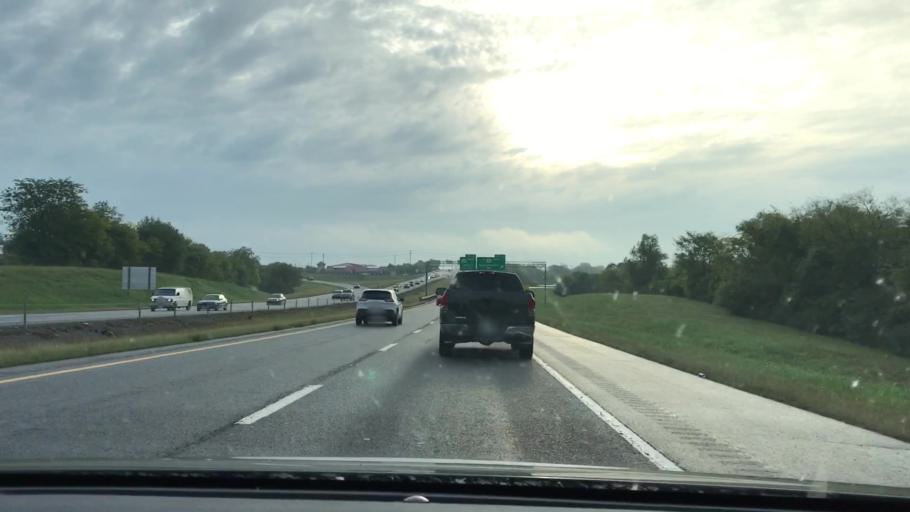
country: US
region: Tennessee
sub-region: Sumner County
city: Hendersonville
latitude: 36.3301
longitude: -86.5705
